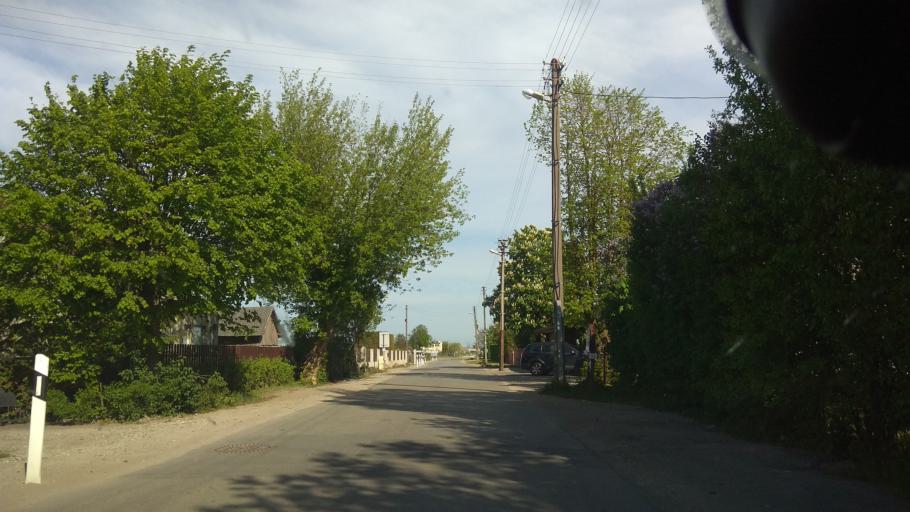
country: LT
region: Klaipedos apskritis
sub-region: Klaipeda
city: Klaipeda
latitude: 55.7563
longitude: 21.1900
